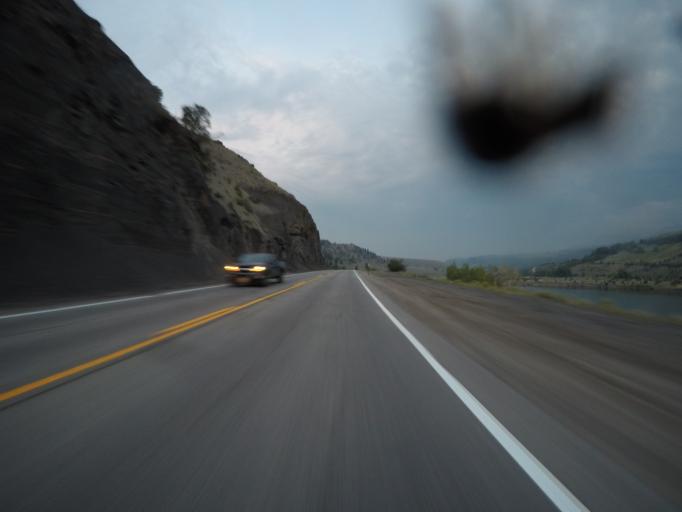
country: US
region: Colorado
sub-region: Grand County
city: Kremmling
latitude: 39.8546
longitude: -106.2390
